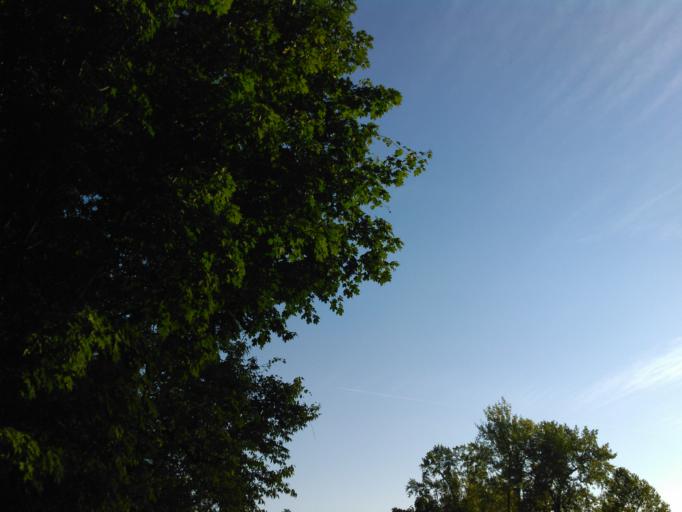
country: US
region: New York
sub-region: Onondaga County
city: Syracuse
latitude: 43.0279
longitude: -76.1154
